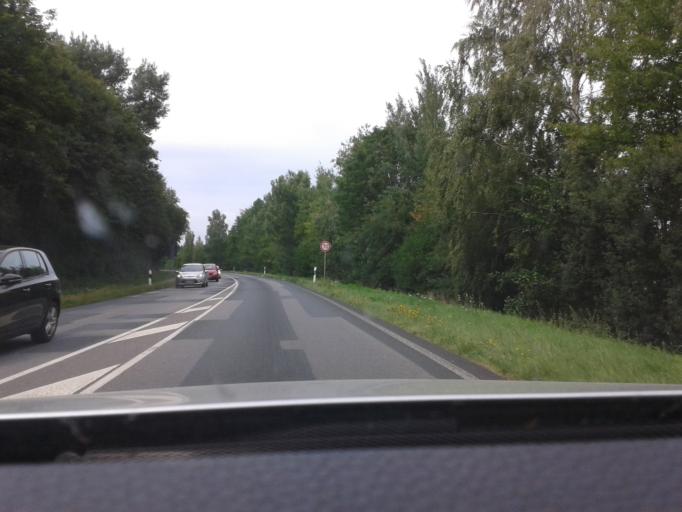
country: DE
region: Lower Saxony
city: Gifhorn
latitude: 52.4853
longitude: 10.5754
